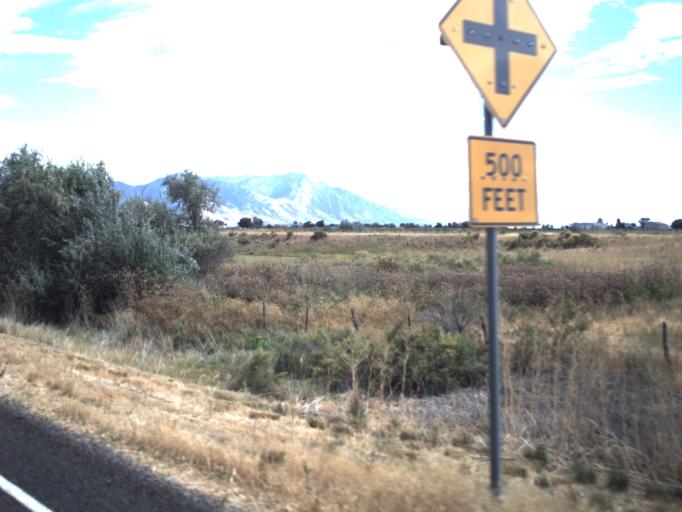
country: US
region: Utah
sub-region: Box Elder County
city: Honeyville
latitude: 41.5657
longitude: -112.1802
